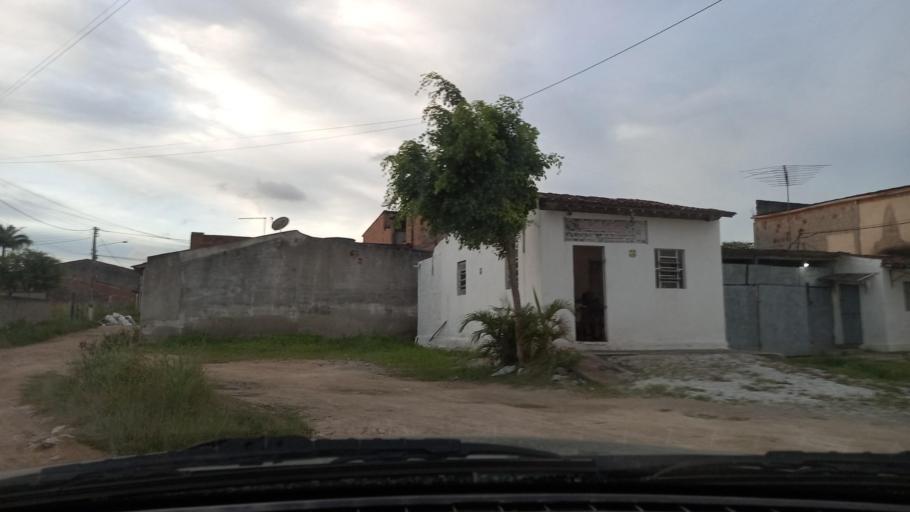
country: BR
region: Pernambuco
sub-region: Gravata
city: Gravata
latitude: -8.1953
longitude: -35.5713
